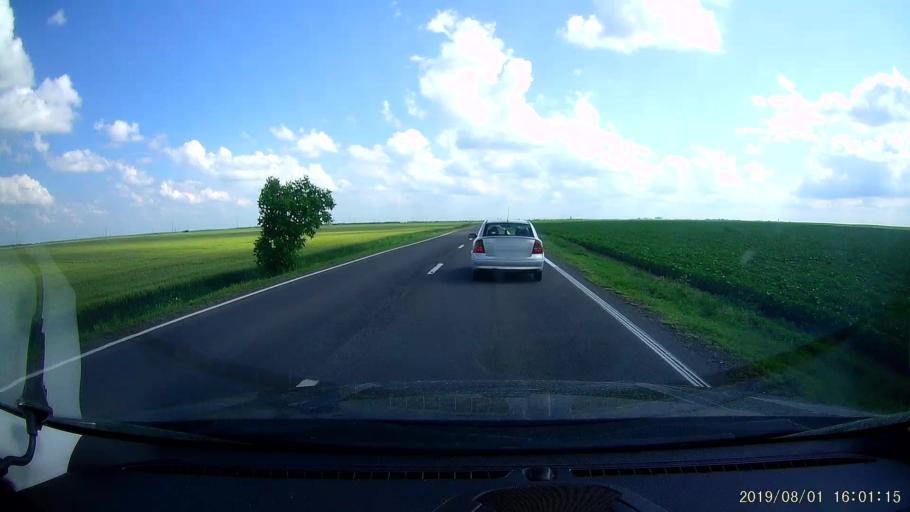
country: RO
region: Ialomita
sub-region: Comuna Ciulnita
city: Ciulnita
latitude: 44.5121
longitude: 27.3900
